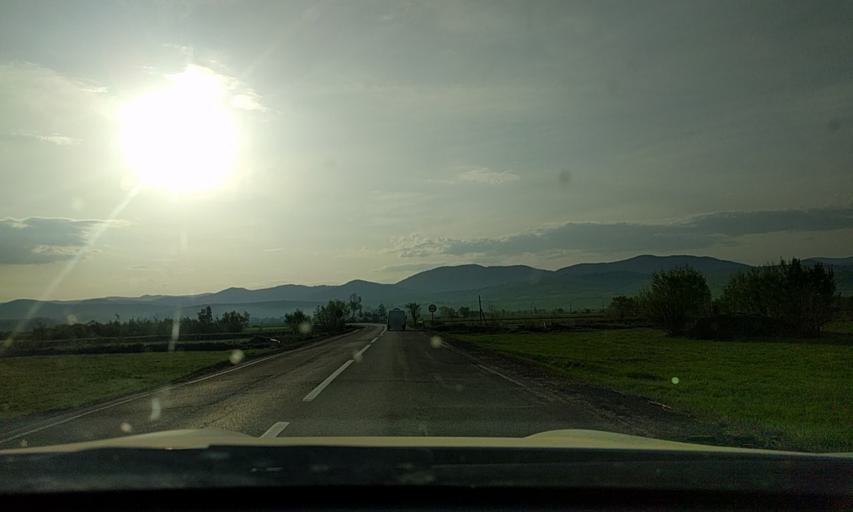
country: RO
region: Covasna
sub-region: Comuna Lemnia
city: Lemnia
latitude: 46.0440
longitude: 26.2725
